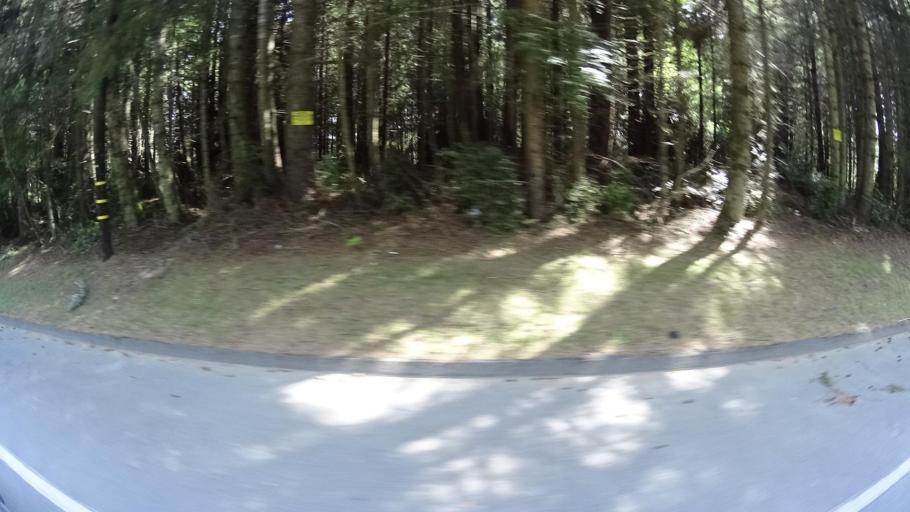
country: US
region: California
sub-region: Humboldt County
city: Cutten
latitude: 40.7546
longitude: -124.1465
